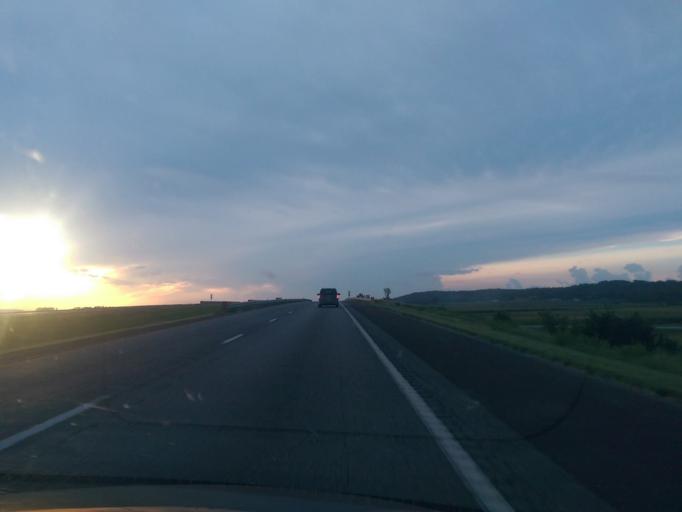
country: US
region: Missouri
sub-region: Atchison County
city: Rock Port
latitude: 40.2512
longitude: -95.4387
